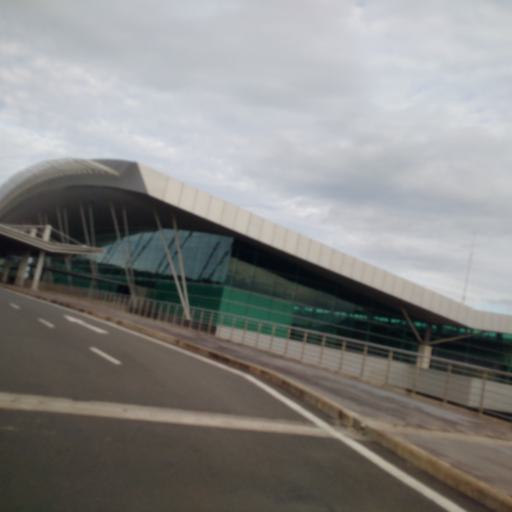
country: VN
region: Kien Giang
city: Duong GJong
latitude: 10.1600
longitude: 103.9978
